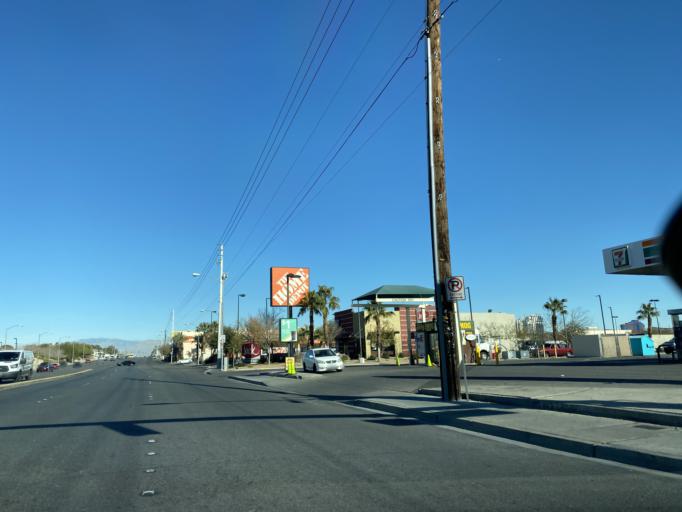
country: US
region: Nevada
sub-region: Clark County
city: Spring Valley
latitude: 36.1011
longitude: -115.2078
